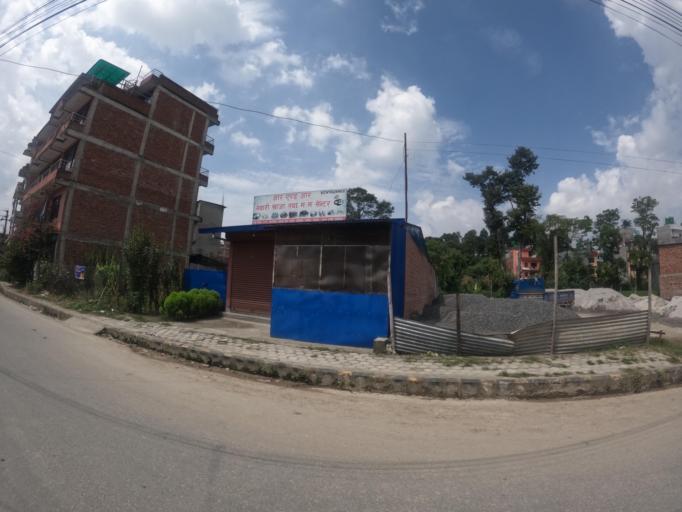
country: NP
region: Central Region
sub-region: Bagmati Zone
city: Bhaktapur
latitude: 27.6786
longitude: 85.3834
